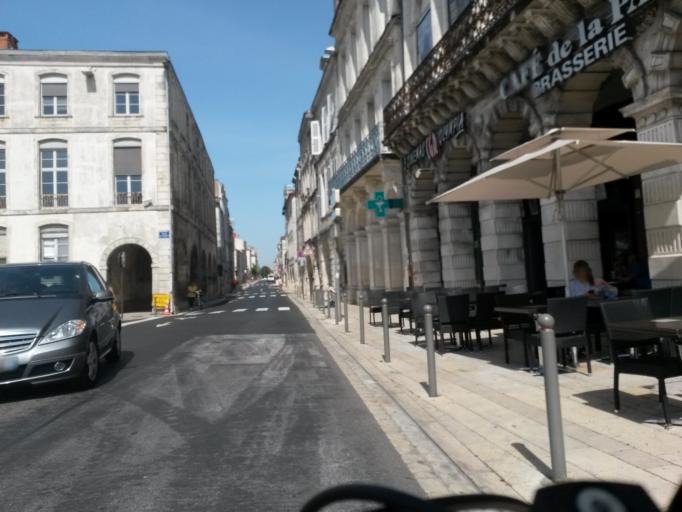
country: FR
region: Poitou-Charentes
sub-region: Departement de la Charente-Maritime
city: La Rochelle
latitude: 46.1626
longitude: -1.1524
